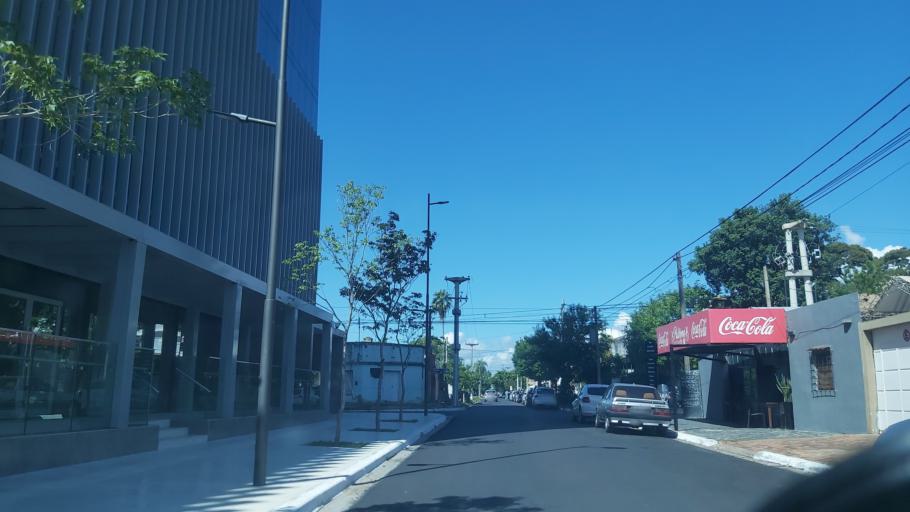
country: AR
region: Corrientes
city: Corrientes
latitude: -27.4753
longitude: -58.8470
